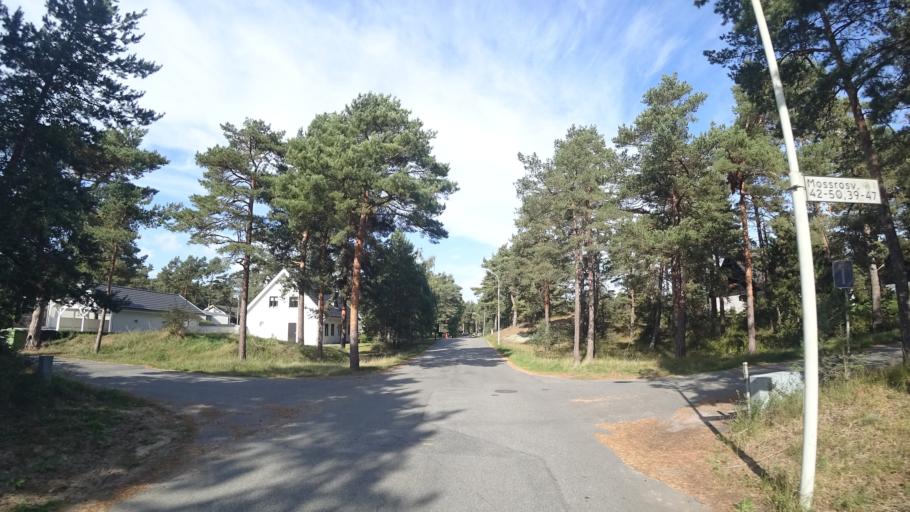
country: SE
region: Skane
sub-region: Kristianstads Kommun
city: Ahus
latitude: 55.9119
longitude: 14.2872
